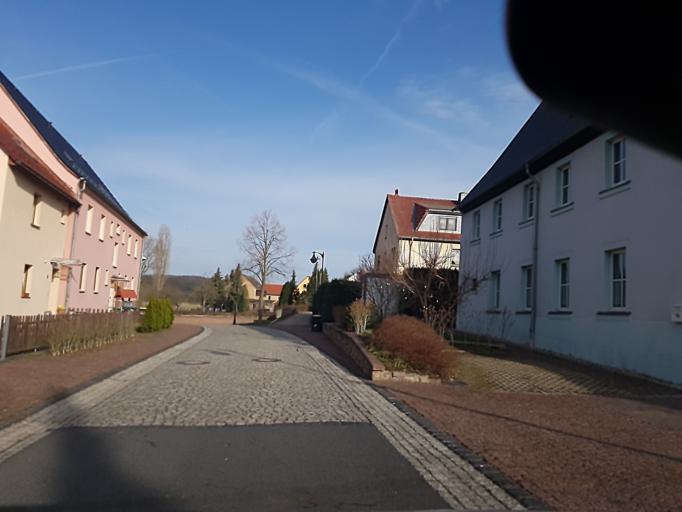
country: DE
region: Saxony
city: Grossweitzschen
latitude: 51.1360
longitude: 13.0262
